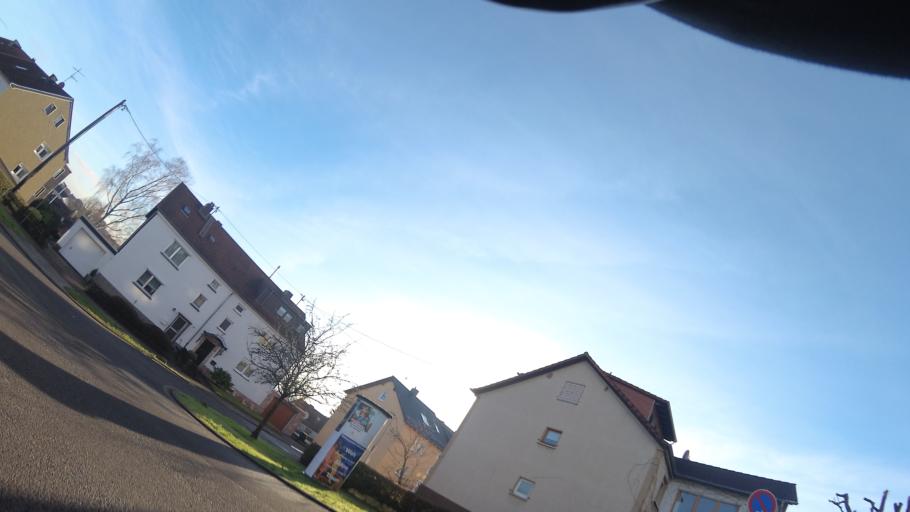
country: DE
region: Saarland
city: Spiesen-Elversberg
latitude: 49.3160
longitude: 7.1225
